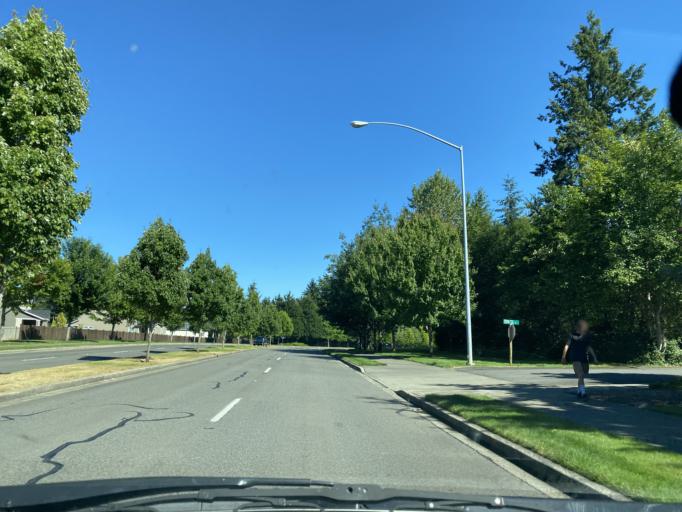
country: US
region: Washington
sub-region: Pierce County
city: McMillin
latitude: 47.1121
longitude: -122.2541
